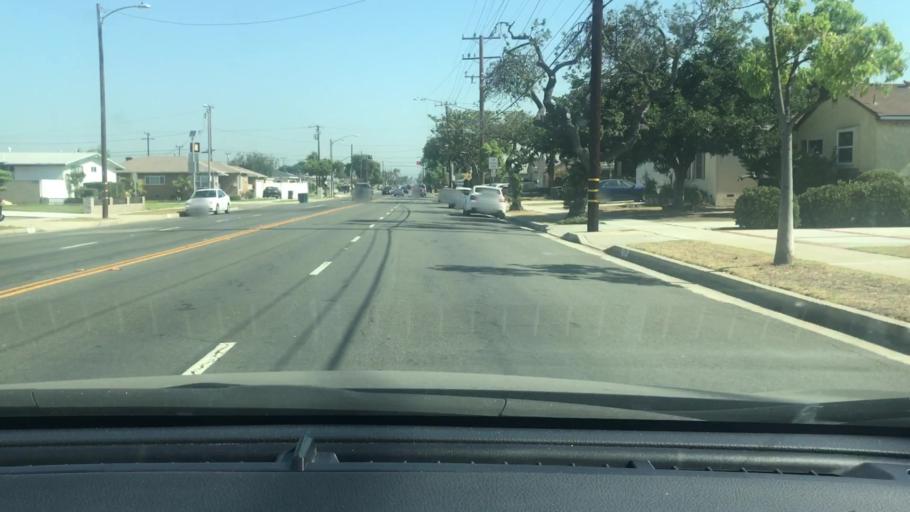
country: US
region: California
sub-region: Los Angeles County
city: Gardena
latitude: 33.8806
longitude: -118.3178
